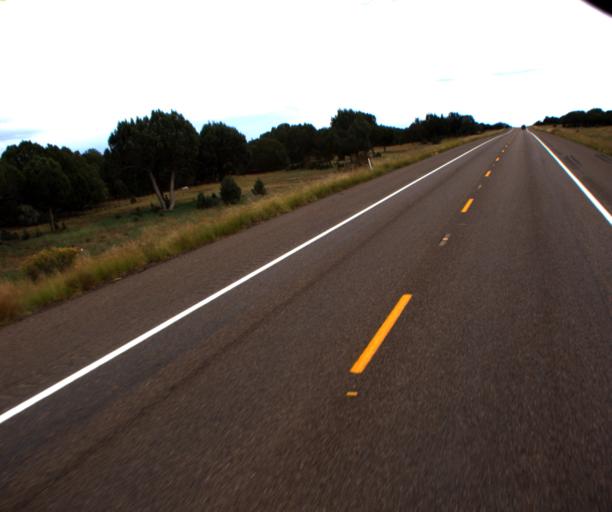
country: US
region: Arizona
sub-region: Navajo County
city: White Mountain Lake
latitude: 34.3129
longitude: -110.0399
